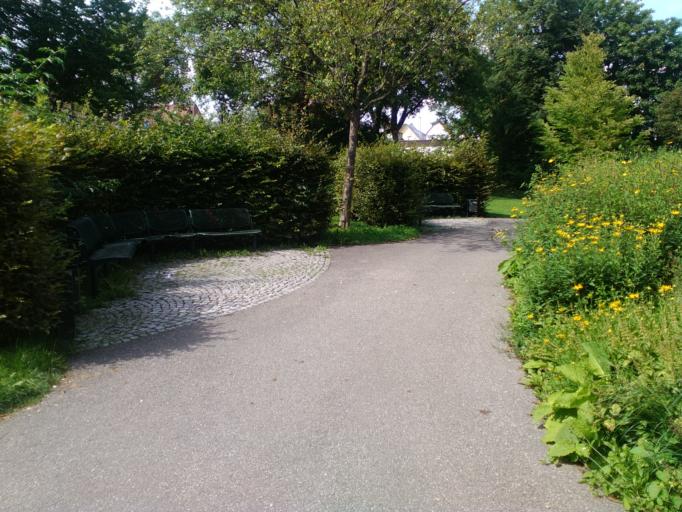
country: DE
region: Baden-Wuerttemberg
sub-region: Regierungsbezirk Stuttgart
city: Leinfelden-Echterdingen
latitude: 48.6991
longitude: 9.1390
